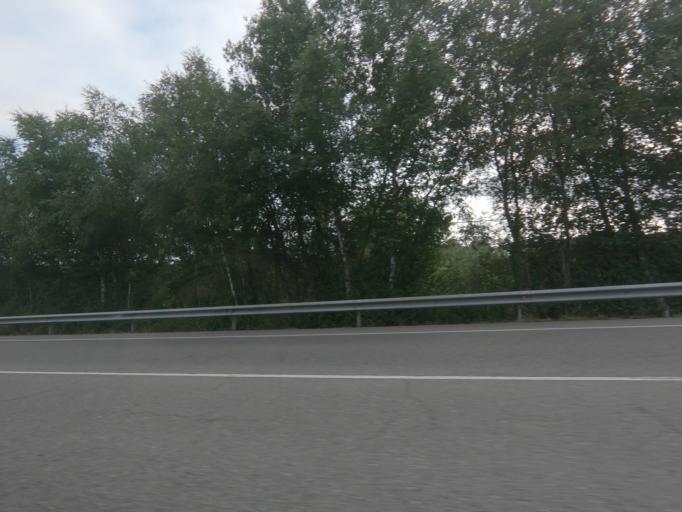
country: ES
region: Galicia
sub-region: Provincia de Ourense
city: Allariz
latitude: 42.2110
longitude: -7.8204
